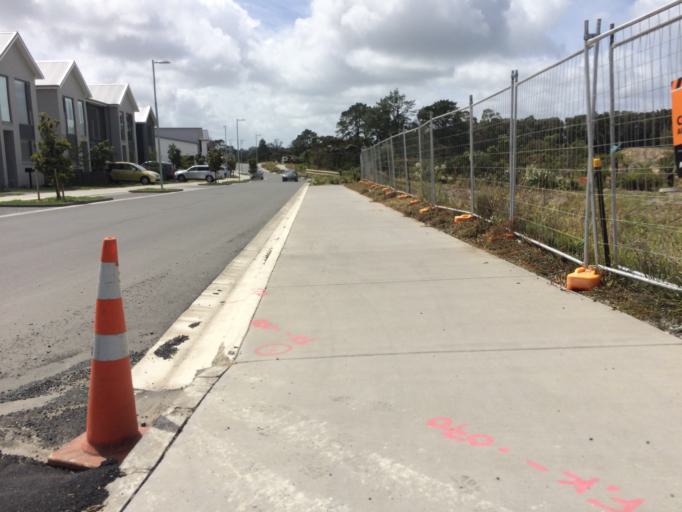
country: NZ
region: Auckland
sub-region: Auckland
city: Rosebank
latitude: -36.7946
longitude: 174.6637
